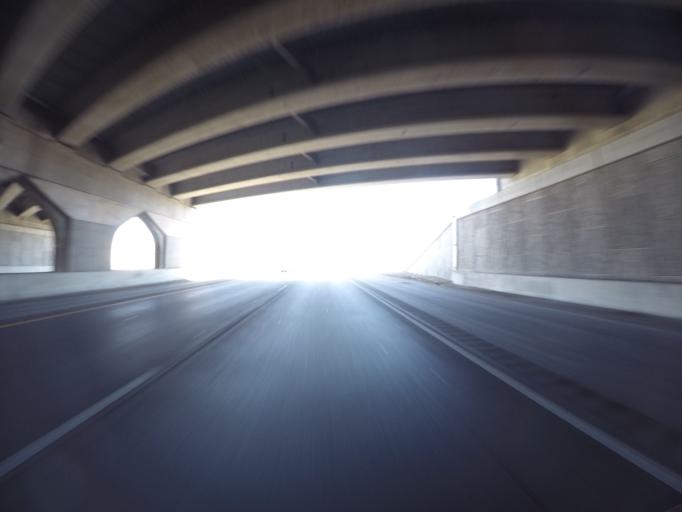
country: US
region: Nebraska
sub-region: Lancaster County
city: Lincoln
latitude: 40.8026
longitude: -96.7445
